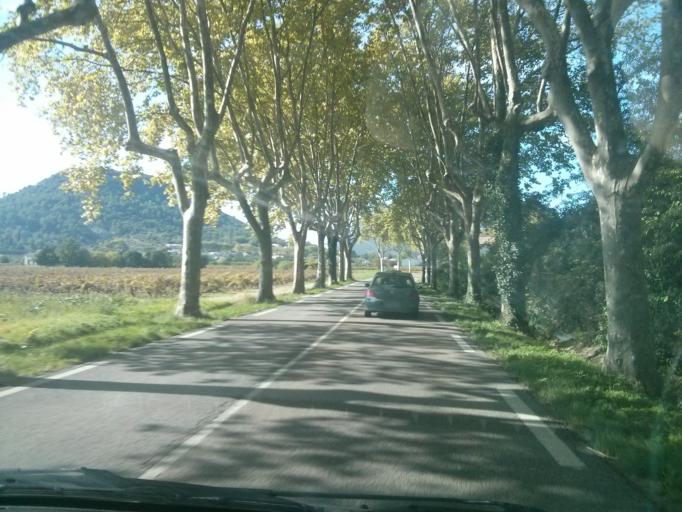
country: FR
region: Languedoc-Roussillon
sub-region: Departement du Gard
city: Saint-Hippolyte-du-Fort
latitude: 43.9558
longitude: 3.8699
